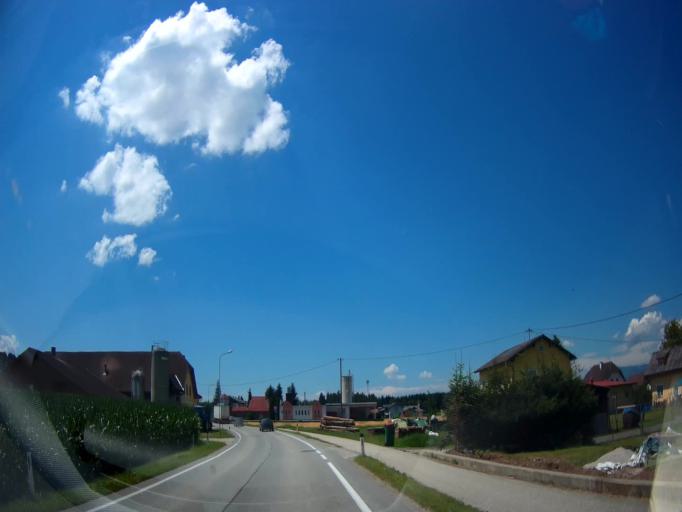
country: AT
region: Carinthia
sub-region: Politischer Bezirk Volkermarkt
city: Globasnitz
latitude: 46.6049
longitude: 14.7171
